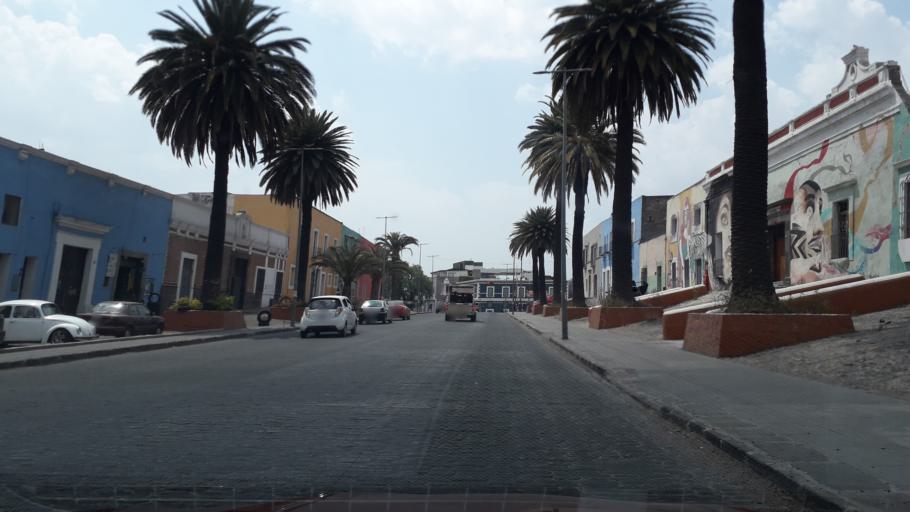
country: MX
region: Puebla
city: Puebla
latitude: 19.0447
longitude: -98.1867
